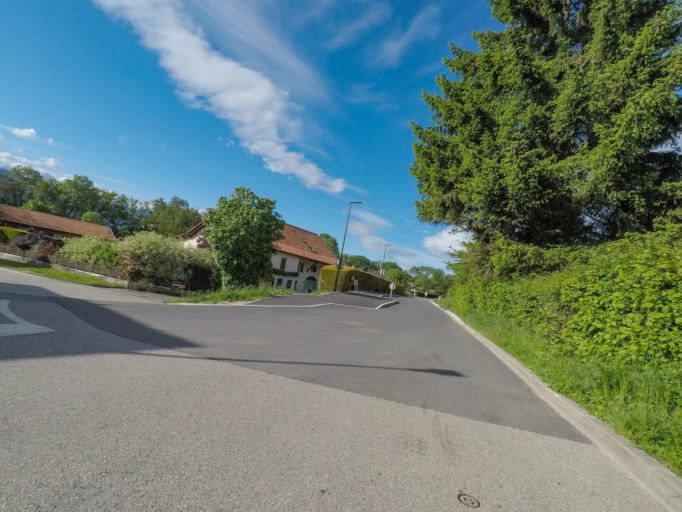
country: FR
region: Rhone-Alpes
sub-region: Departement de l'Ain
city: Ornex
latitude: 46.2661
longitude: 6.0722
